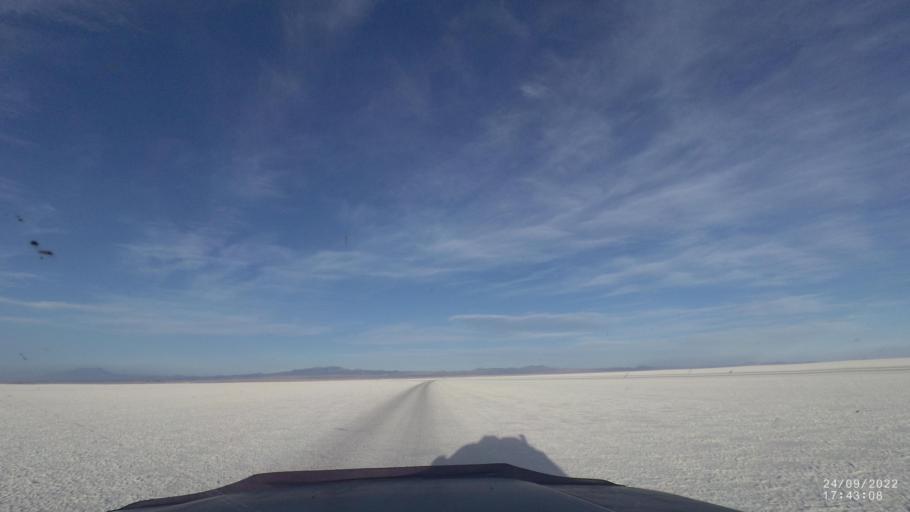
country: BO
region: Potosi
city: Colchani
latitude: -20.3340
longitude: -67.0653
